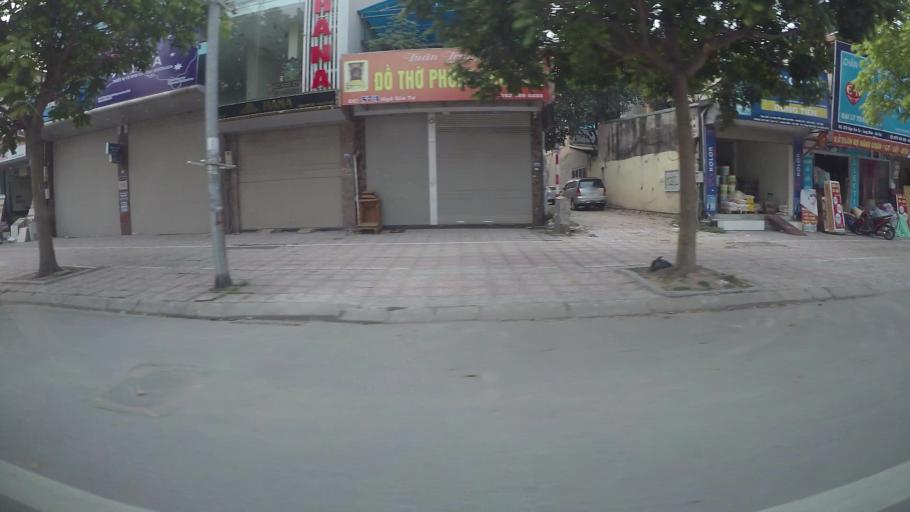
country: VN
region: Ha Noi
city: Trau Quy
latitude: 21.0661
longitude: 105.8984
